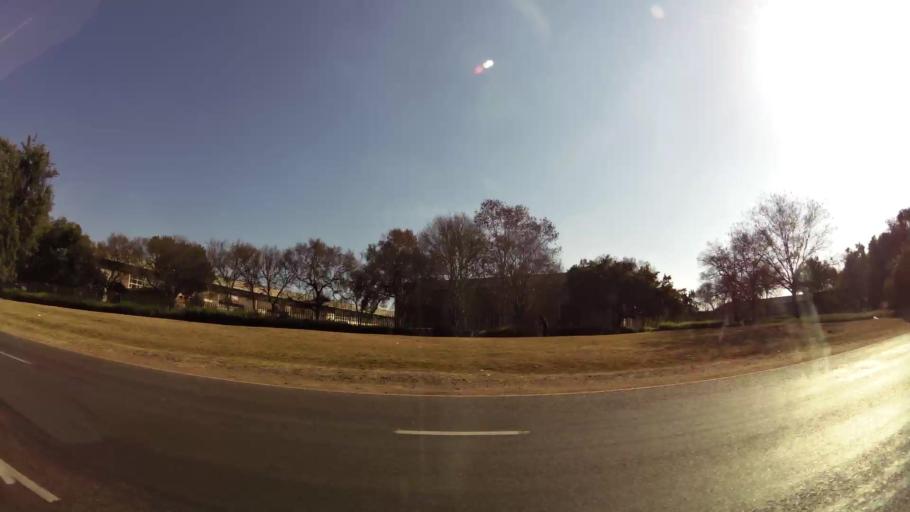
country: ZA
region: Gauteng
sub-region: City of Tshwane Metropolitan Municipality
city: Pretoria
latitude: -25.7184
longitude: 28.1694
